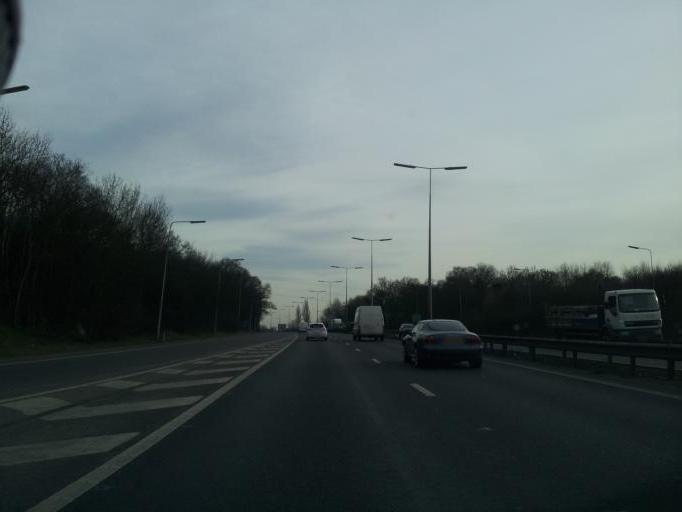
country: GB
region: England
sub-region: Hertfordshire
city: Hatfield
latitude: 51.7388
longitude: -0.2383
